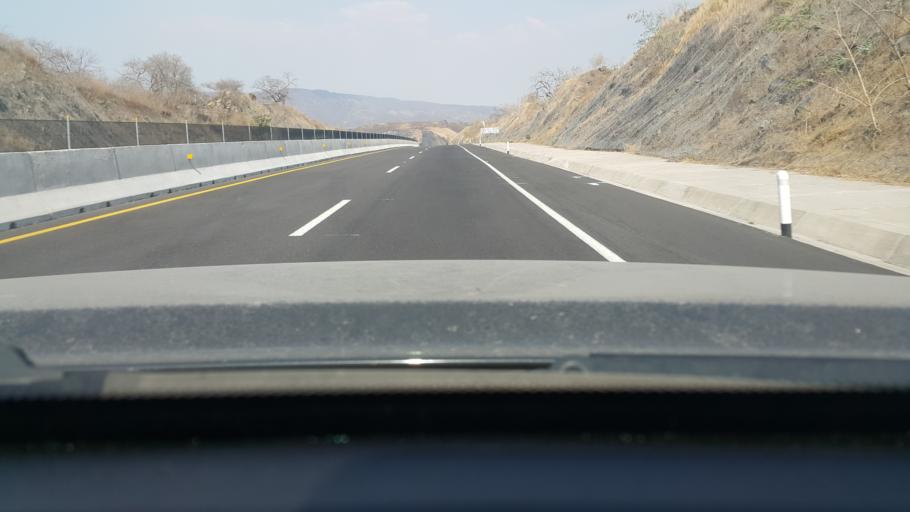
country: MX
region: Nayarit
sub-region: Ahuacatlan
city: Ahuacatlan
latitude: 21.0670
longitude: -104.4676
